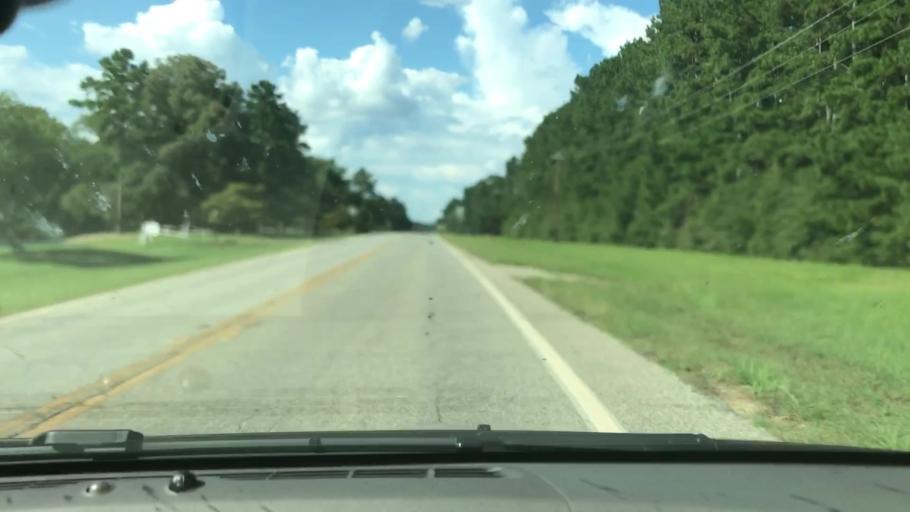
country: US
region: Georgia
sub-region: Clay County
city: Fort Gaines
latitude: 31.6321
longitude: -85.0442
